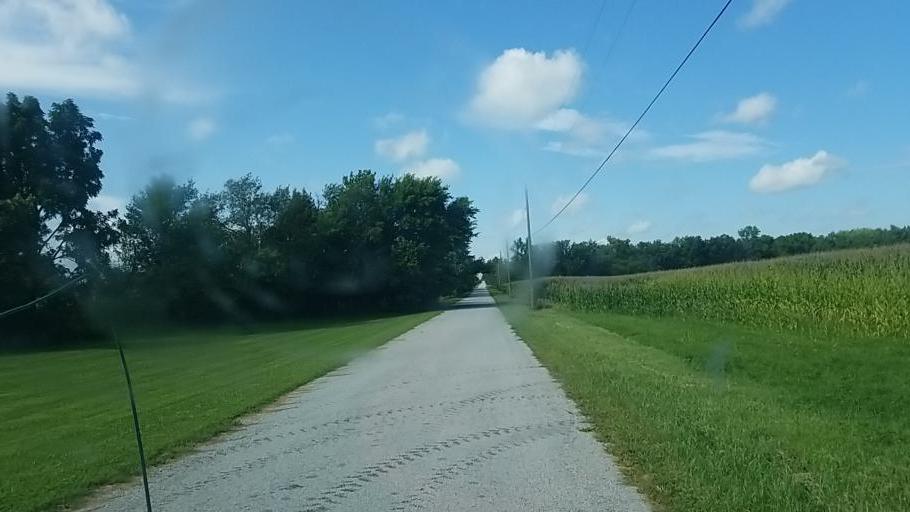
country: US
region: Ohio
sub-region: Hardin County
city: Kenton
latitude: 40.6699
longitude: -83.5476
